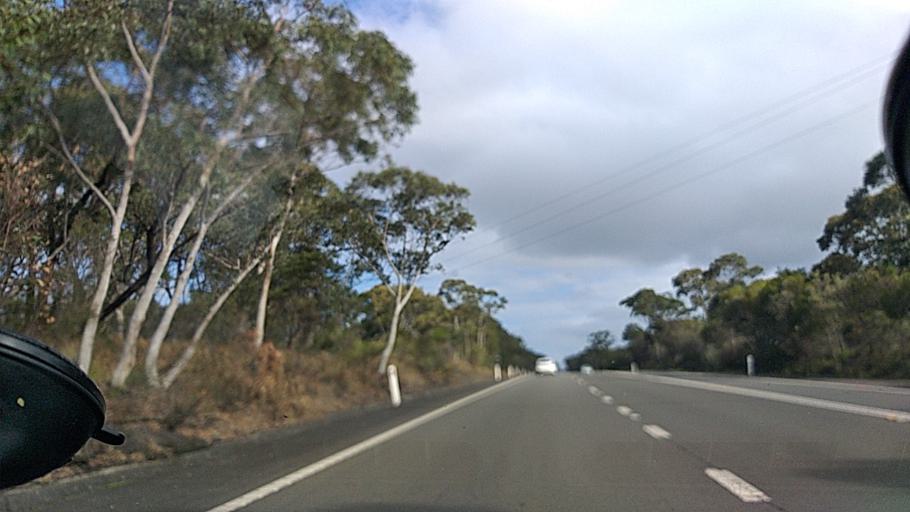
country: AU
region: New South Wales
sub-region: Wollongong
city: Bulli
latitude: -34.2882
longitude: 150.9008
